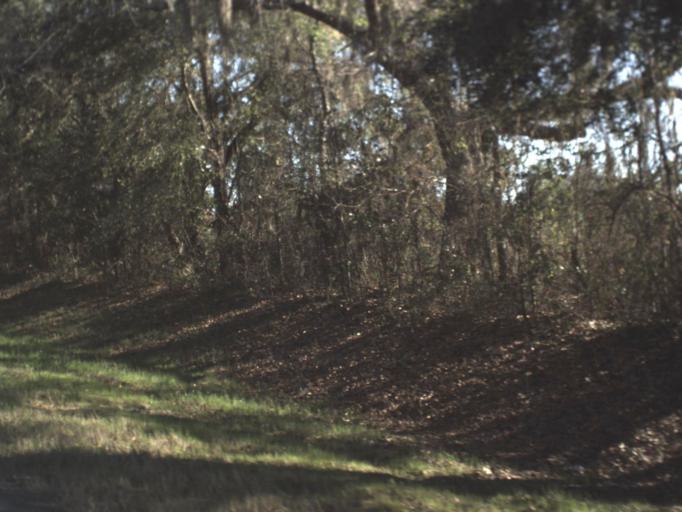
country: US
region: Georgia
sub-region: Brooks County
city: Quitman
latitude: 30.6545
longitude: -83.6420
